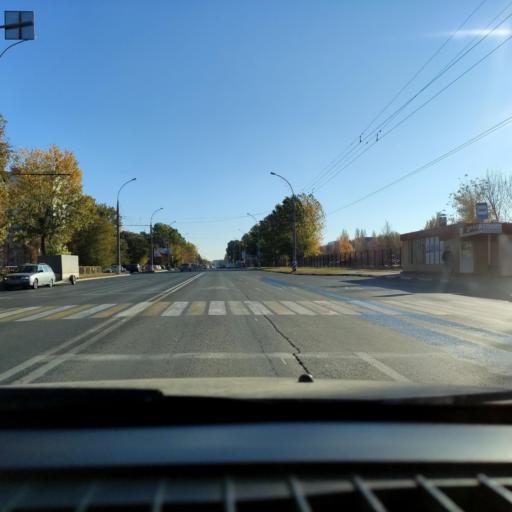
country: RU
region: Samara
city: Tol'yatti
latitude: 53.5081
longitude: 49.2596
